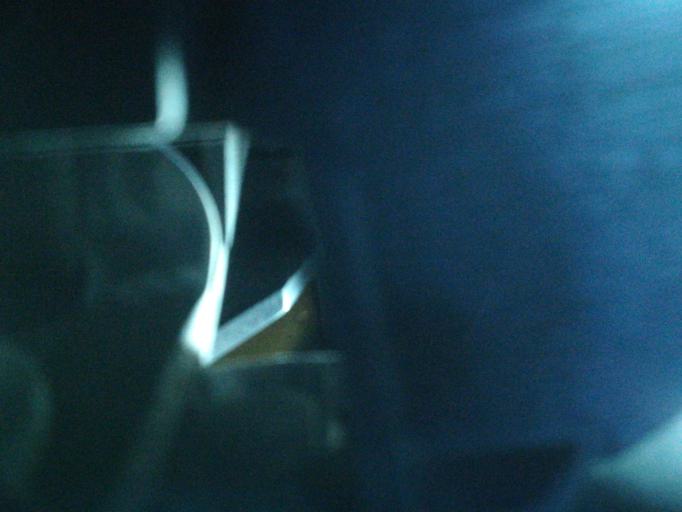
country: TR
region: Adana
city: Adana
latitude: 37.0539
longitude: 35.3632
